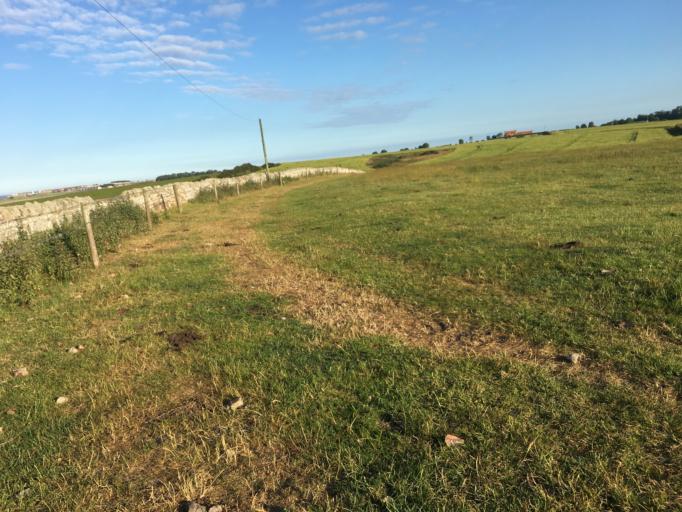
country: GB
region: England
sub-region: Northumberland
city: Bamburgh
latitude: 55.5976
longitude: -1.6946
